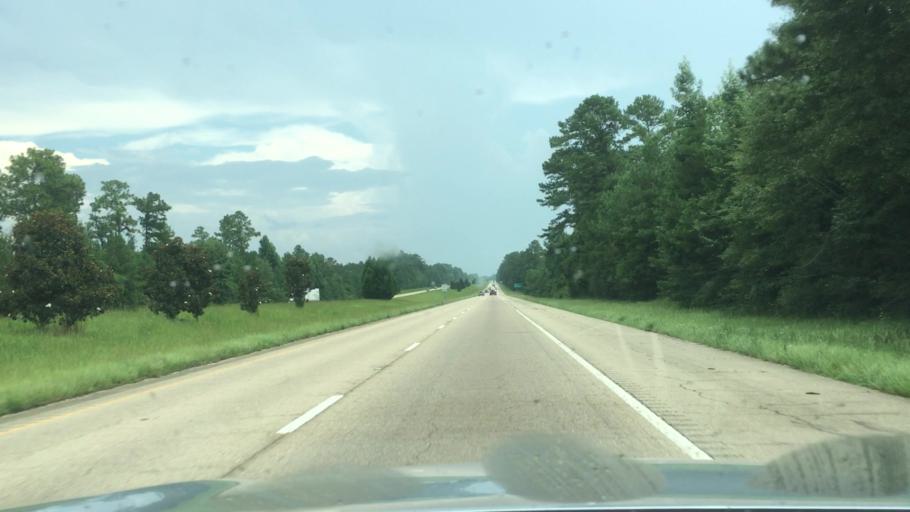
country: US
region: Mississippi
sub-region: Lamar County
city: Lumberton
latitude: 31.0102
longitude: -89.4138
